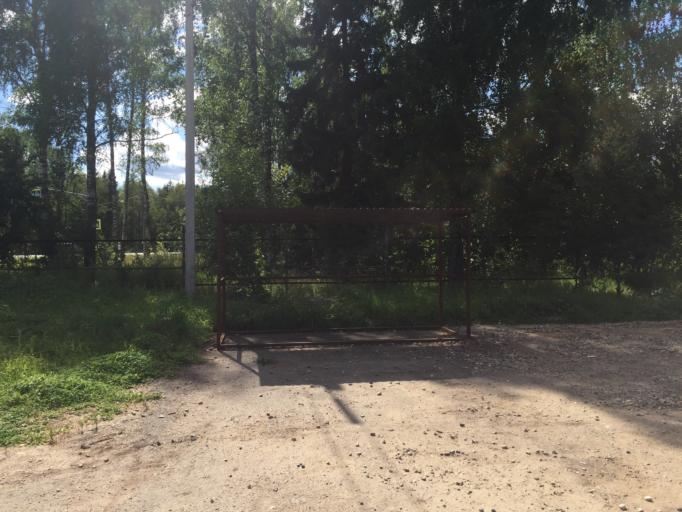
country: RU
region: Jaroslavl
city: Tunoshna
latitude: 57.5468
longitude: 40.1583
